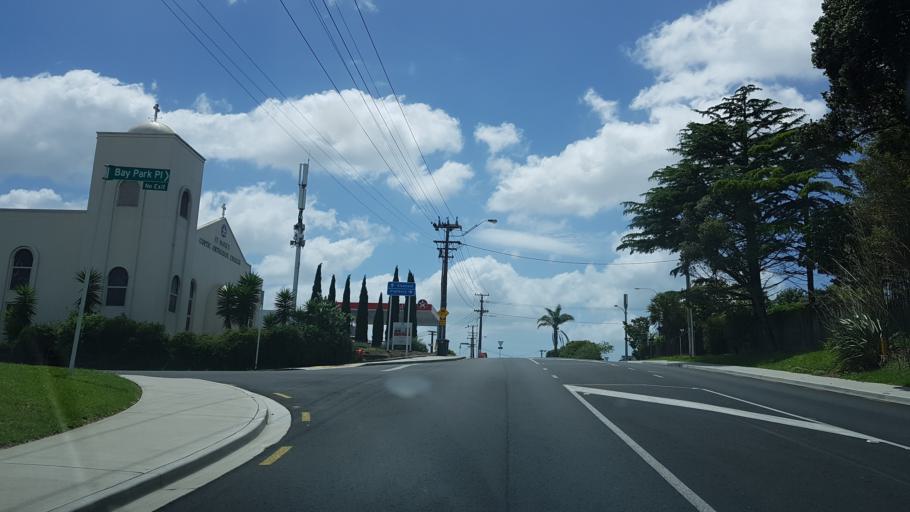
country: NZ
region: Auckland
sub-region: Auckland
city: North Shore
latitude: -36.7883
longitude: 174.6983
